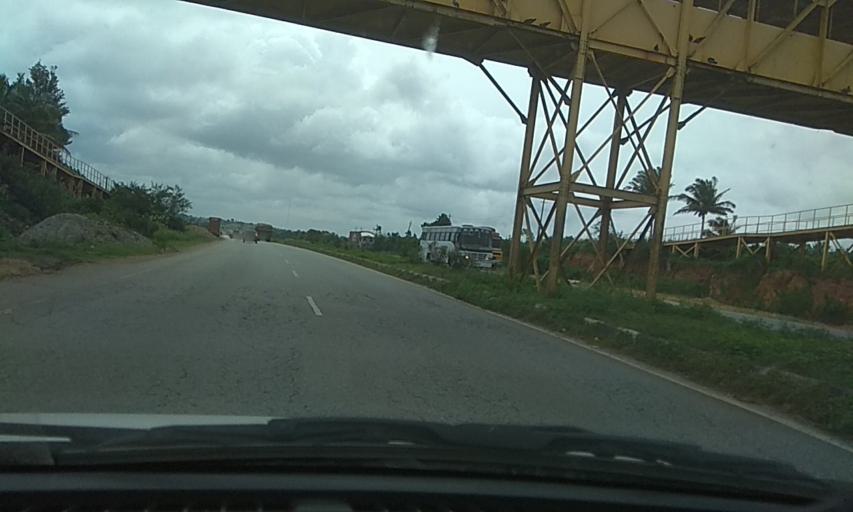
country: IN
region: Karnataka
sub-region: Davanagere
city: Mayakonda
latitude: 14.3669
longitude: 76.1503
